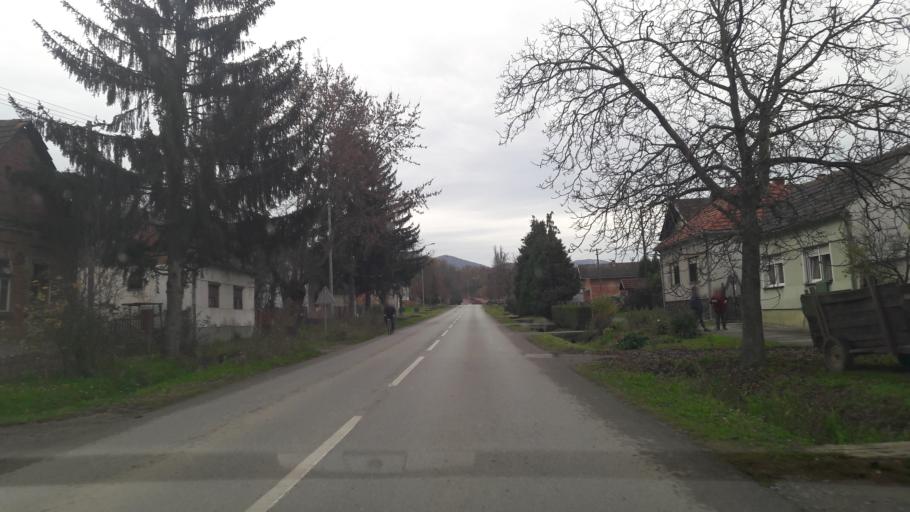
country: HR
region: Virovitick-Podravska
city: Orahovica
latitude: 45.5387
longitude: 17.8940
